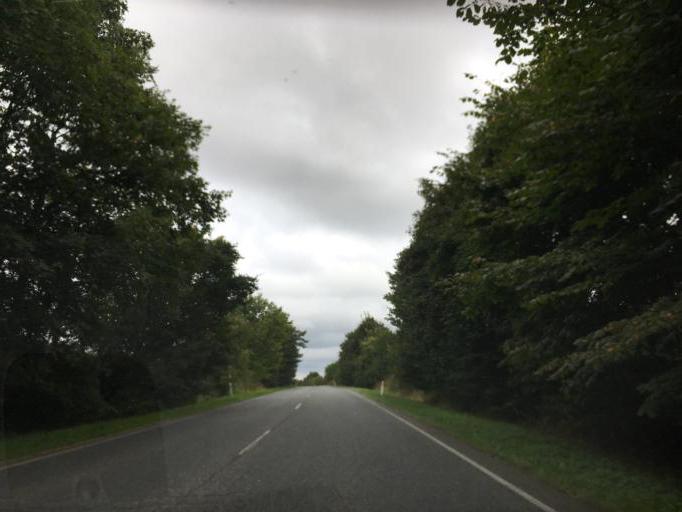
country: DK
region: South Denmark
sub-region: Kolding Kommune
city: Kolding
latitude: 55.5754
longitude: 9.4995
